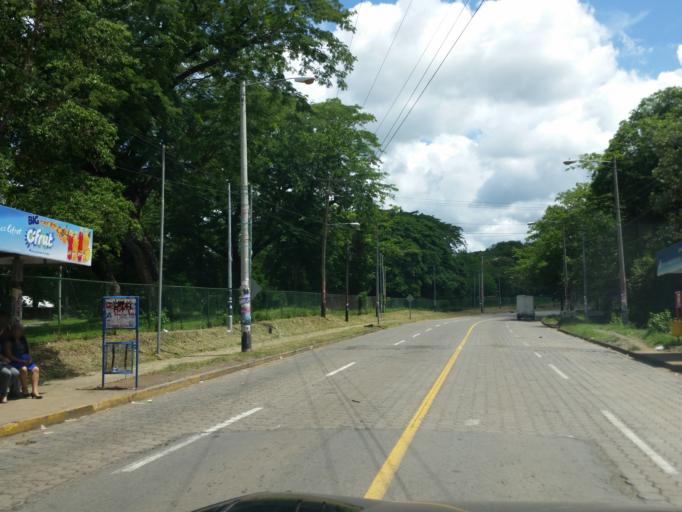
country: NI
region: Managua
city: Managua
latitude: 12.1120
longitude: -86.2719
